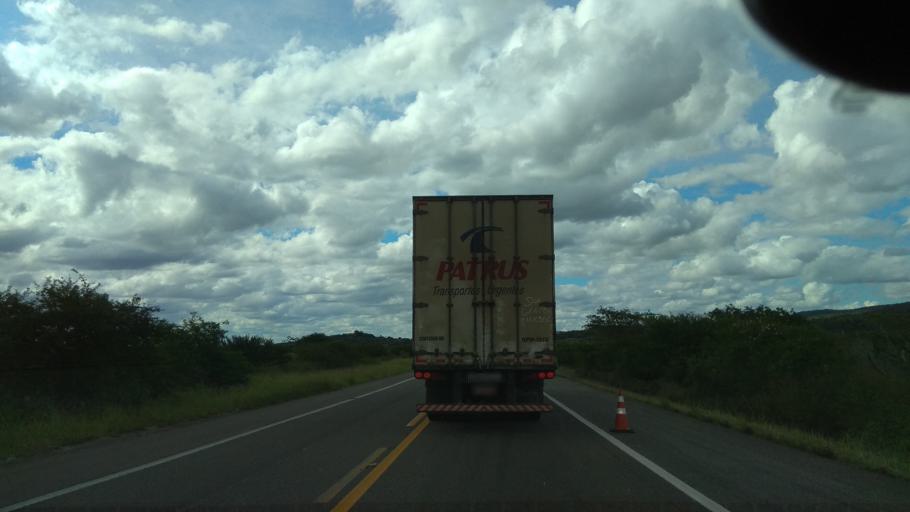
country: BR
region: Bahia
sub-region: Santa Ines
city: Santa Ines
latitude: -12.9874
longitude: -39.9449
